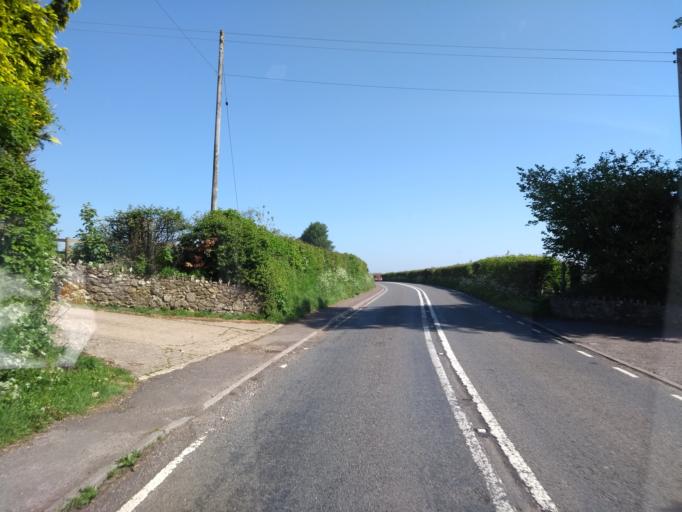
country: GB
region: England
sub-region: Somerset
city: Chard
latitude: 50.8517
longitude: -2.9574
